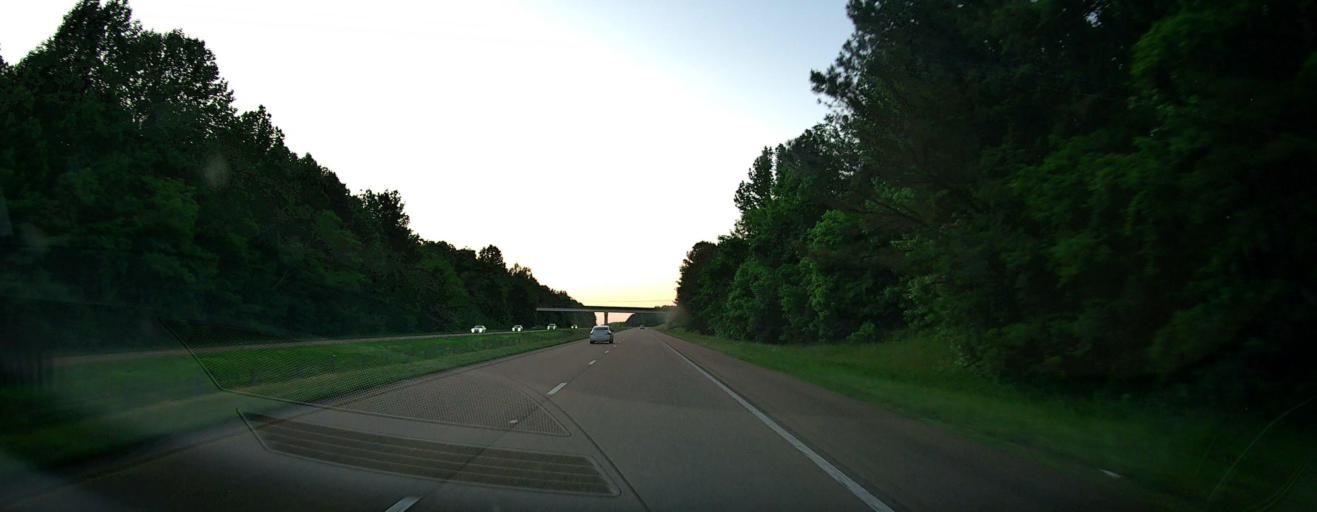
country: US
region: Mississippi
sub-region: Union County
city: New Albany
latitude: 34.4260
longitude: -88.9586
